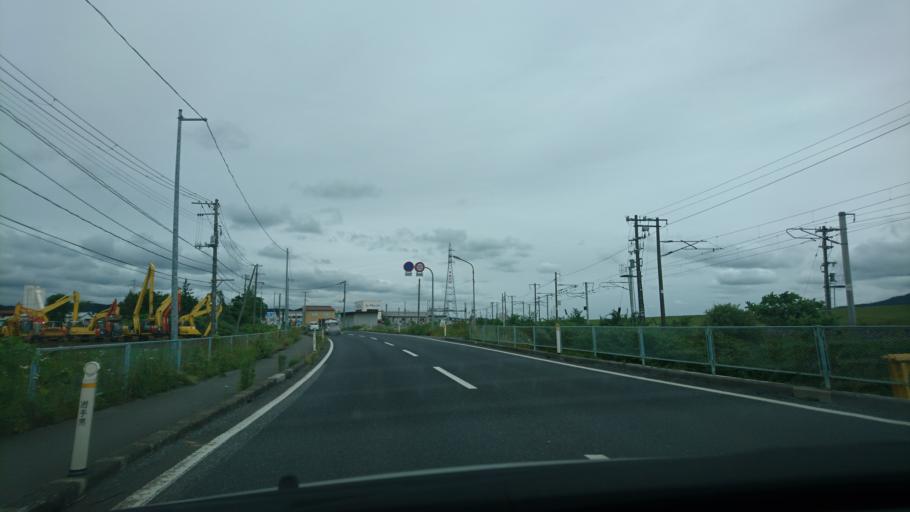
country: JP
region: Iwate
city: Ichinoseki
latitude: 38.9612
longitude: 141.1279
